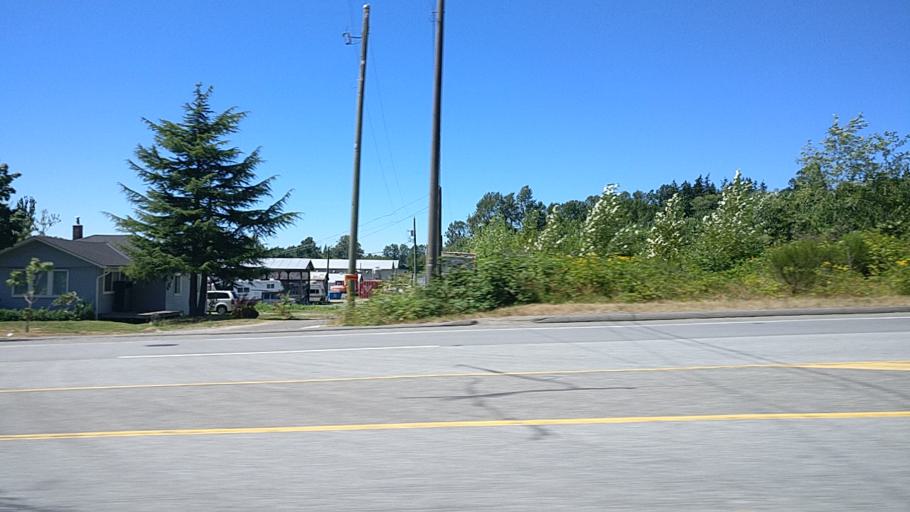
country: US
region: Washington
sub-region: Whatcom County
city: Blaine
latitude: 49.0303
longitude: -122.7351
